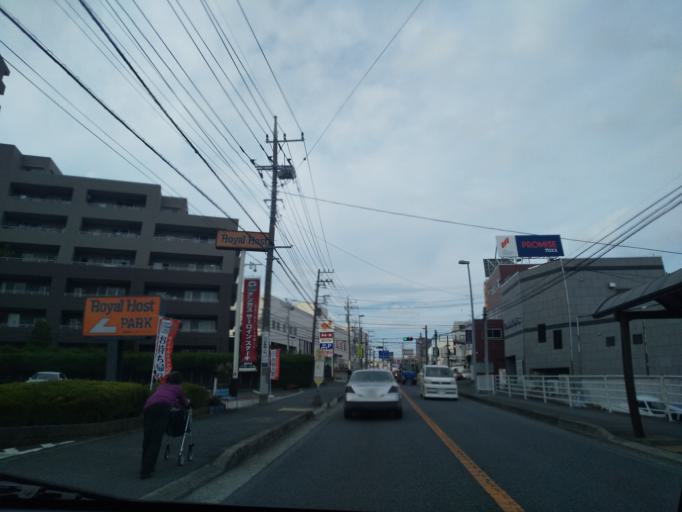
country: JP
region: Kanagawa
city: Zama
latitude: 35.5068
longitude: 139.4129
